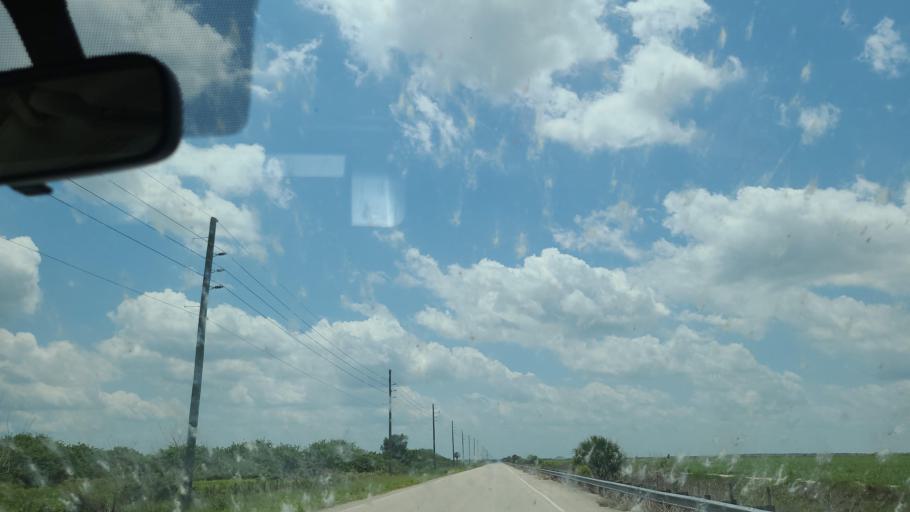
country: US
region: Florida
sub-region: Glades County
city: Buckhead Ridge
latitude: 27.1827
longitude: -81.0939
